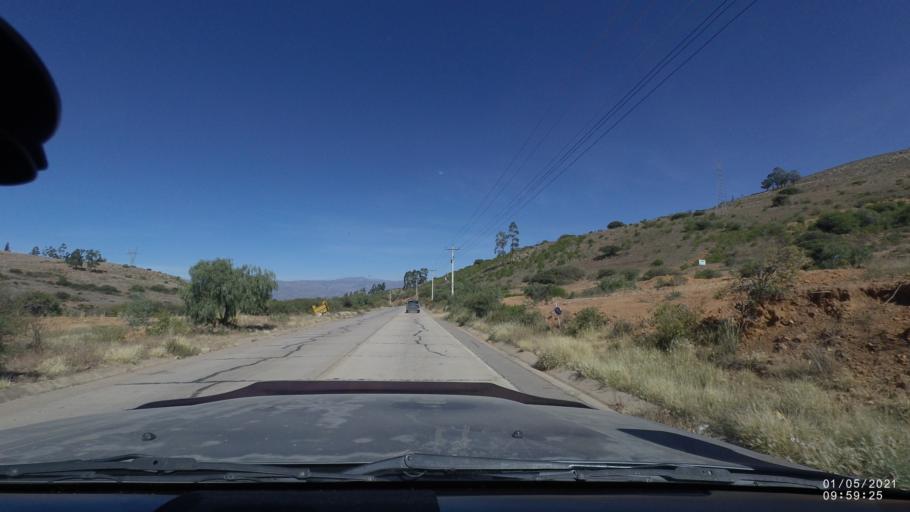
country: BO
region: Cochabamba
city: Cochabamba
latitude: -17.5257
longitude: -66.1887
